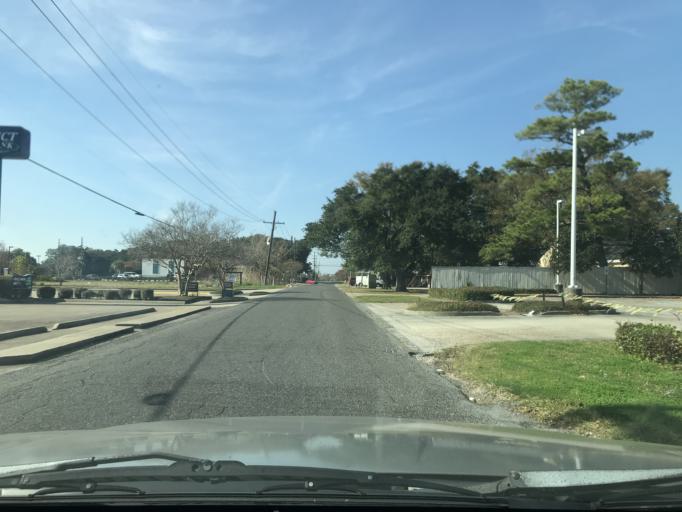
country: US
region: Louisiana
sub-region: Jefferson Parish
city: Marrero
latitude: 29.8933
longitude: -90.0979
